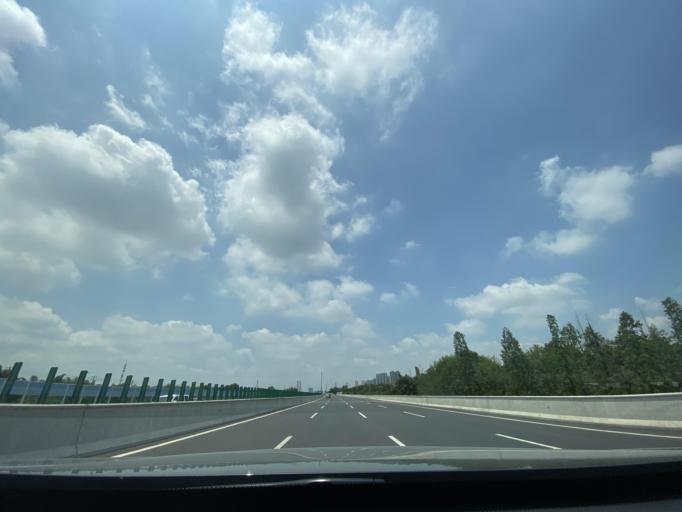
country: CN
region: Sichuan
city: Chengdu
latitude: 30.5826
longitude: 104.1298
